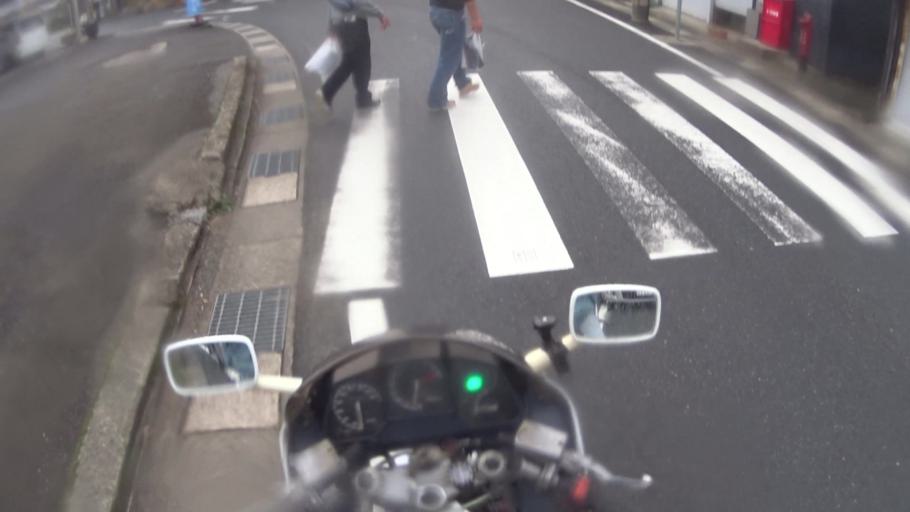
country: JP
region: Kyoto
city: Miyazu
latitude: 35.5476
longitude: 135.2352
